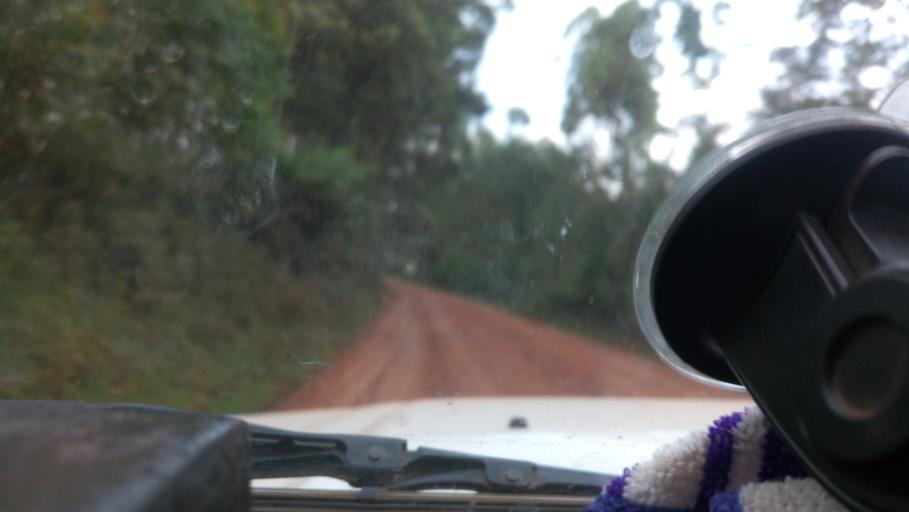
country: KE
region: Kericho
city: Litein
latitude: -0.5829
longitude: 35.1368
